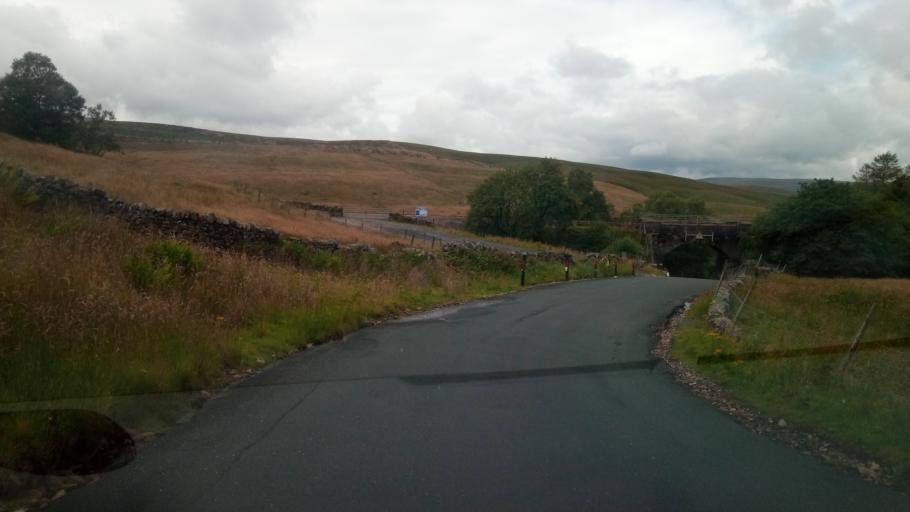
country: GB
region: England
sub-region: North Yorkshire
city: Ingleton
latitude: 54.2531
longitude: -2.3420
